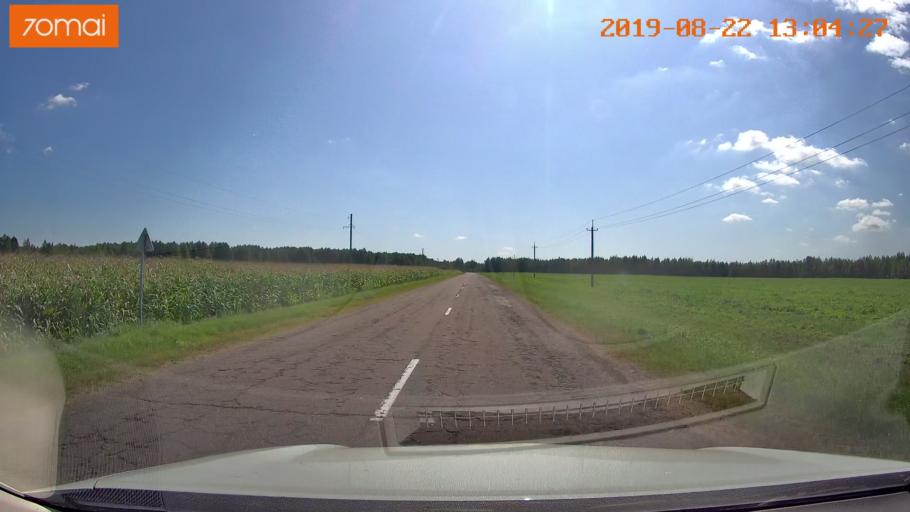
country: BY
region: Minsk
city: Prawdzinski
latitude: 53.3705
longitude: 27.8261
